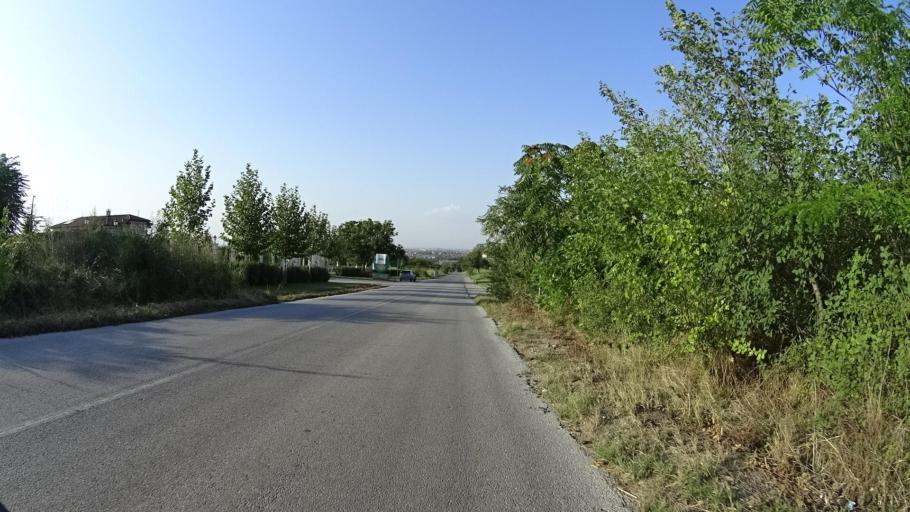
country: BG
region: Plovdiv
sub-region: Obshtina Plovdiv
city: Plovdiv
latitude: 42.0774
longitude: 24.7022
